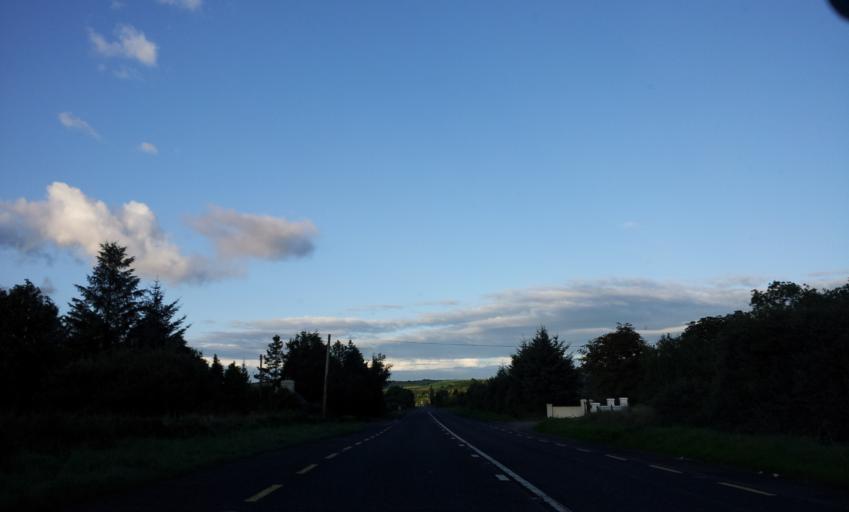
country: IE
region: Munster
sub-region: County Limerick
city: Abbeyfeale
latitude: 52.3890
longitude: -9.1987
